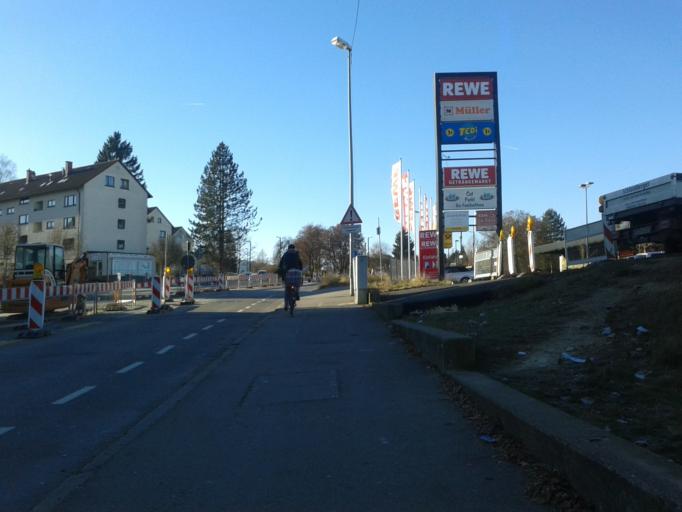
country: DE
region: Baden-Wuerttemberg
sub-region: Tuebingen Region
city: Ulm
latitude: 48.3861
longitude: 9.9666
